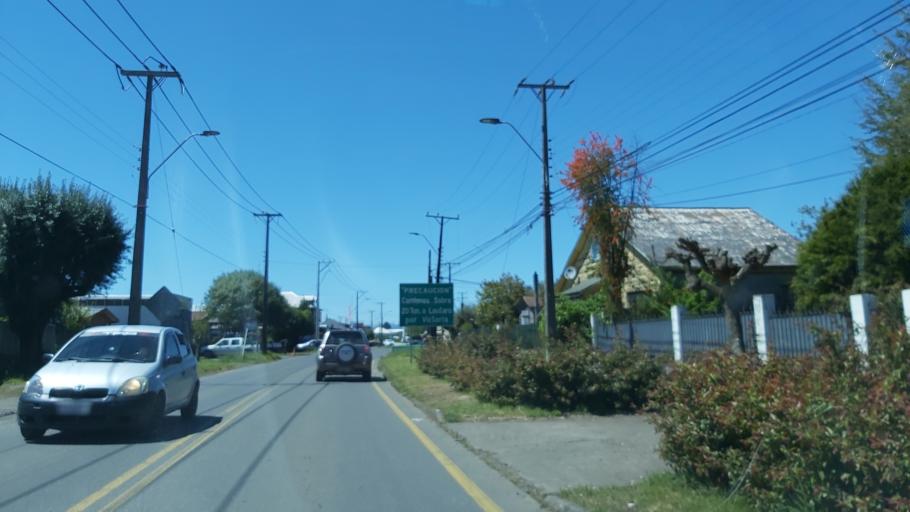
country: CL
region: Araucania
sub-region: Provincia de Cautin
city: Vilcun
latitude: -38.4353
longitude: -71.8993
